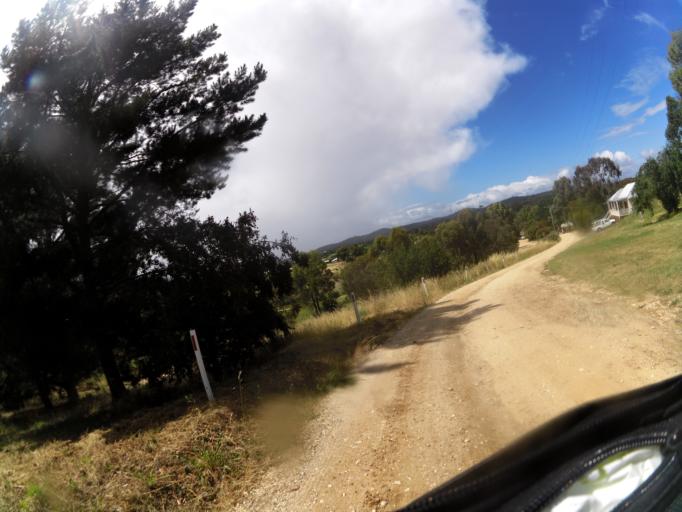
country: AU
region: Victoria
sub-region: Mount Alexander
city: Castlemaine
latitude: -37.0673
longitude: 144.2278
